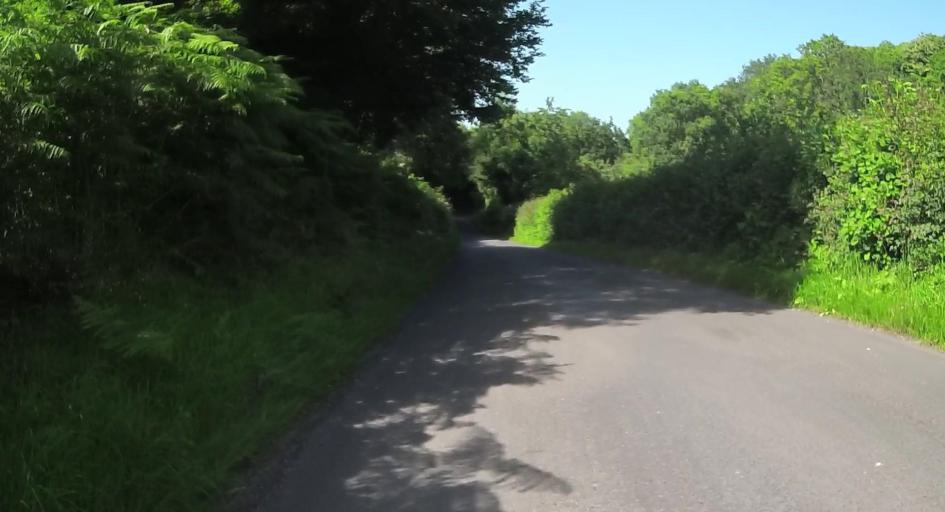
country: GB
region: England
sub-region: Hampshire
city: Kingsley
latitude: 51.1546
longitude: -0.8926
